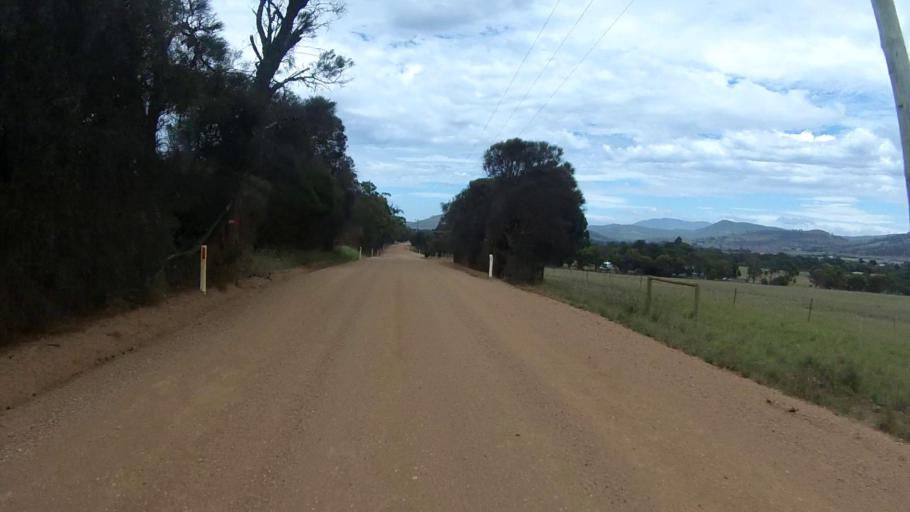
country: AU
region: Tasmania
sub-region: Clarence
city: Cambridge
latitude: -42.7045
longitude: 147.4572
